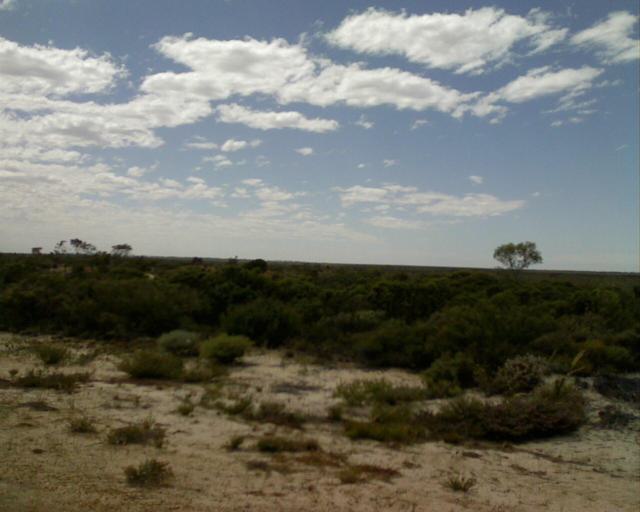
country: AU
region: Western Australia
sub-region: Moora
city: Moora
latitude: -30.0522
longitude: 115.6905
